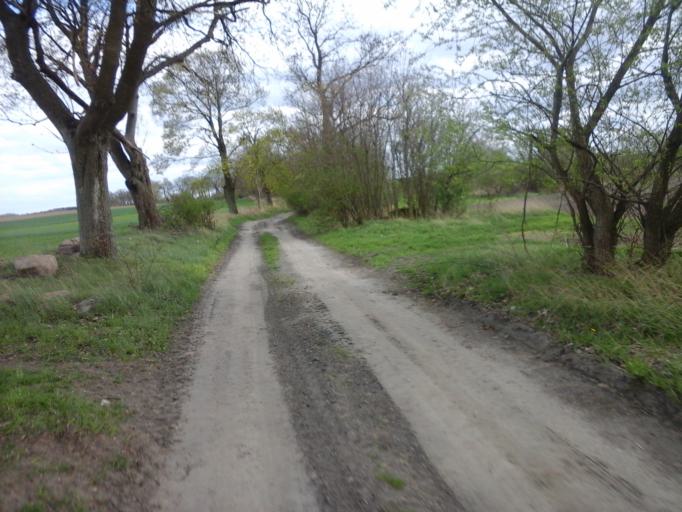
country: PL
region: West Pomeranian Voivodeship
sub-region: Powiat choszczenski
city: Krzecin
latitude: 53.1125
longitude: 15.5037
